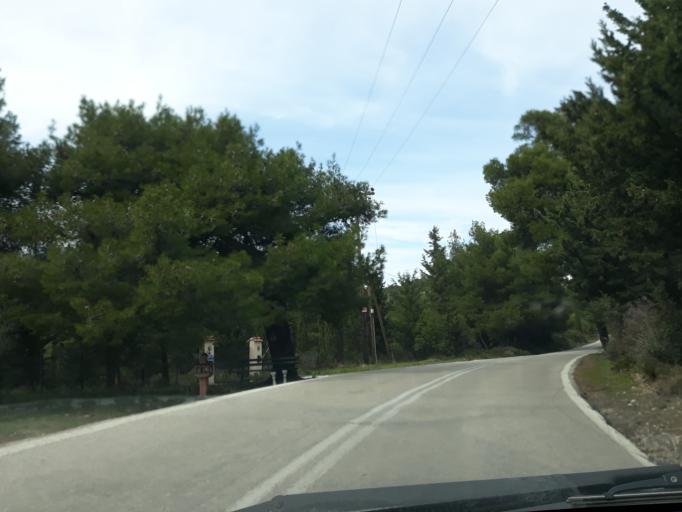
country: GR
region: Attica
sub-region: Nomarchia Anatolikis Attikis
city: Varybobi
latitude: 38.1385
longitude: 23.7930
